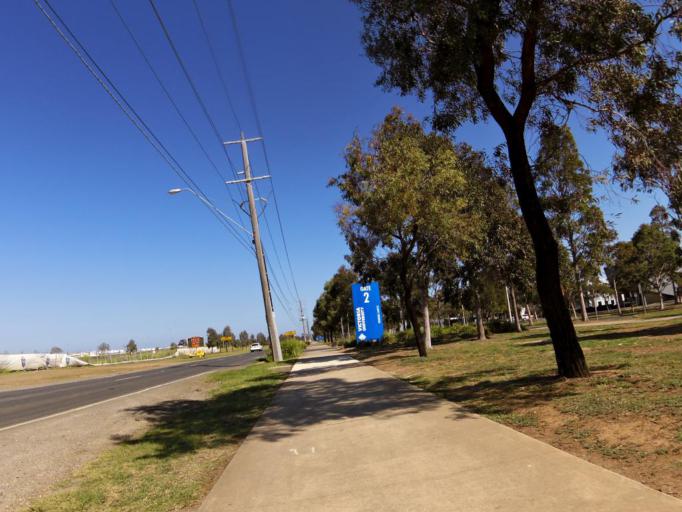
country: AU
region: Victoria
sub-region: Wyndham
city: Hoppers Crossing
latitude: -37.8875
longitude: 144.7004
